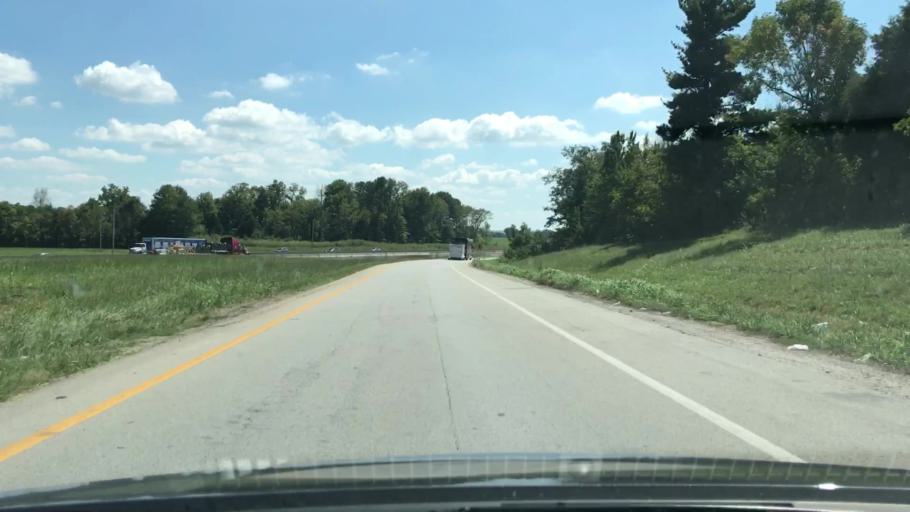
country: US
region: Kentucky
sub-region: Hardin County
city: Elizabethtown
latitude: 37.5947
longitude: -85.8702
